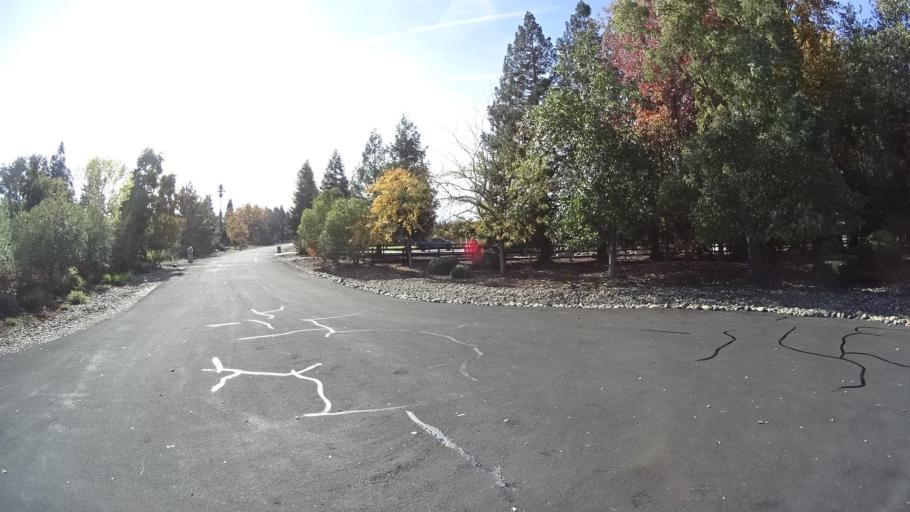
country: US
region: California
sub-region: Sacramento County
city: Wilton
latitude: 38.4362
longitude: -121.2839
